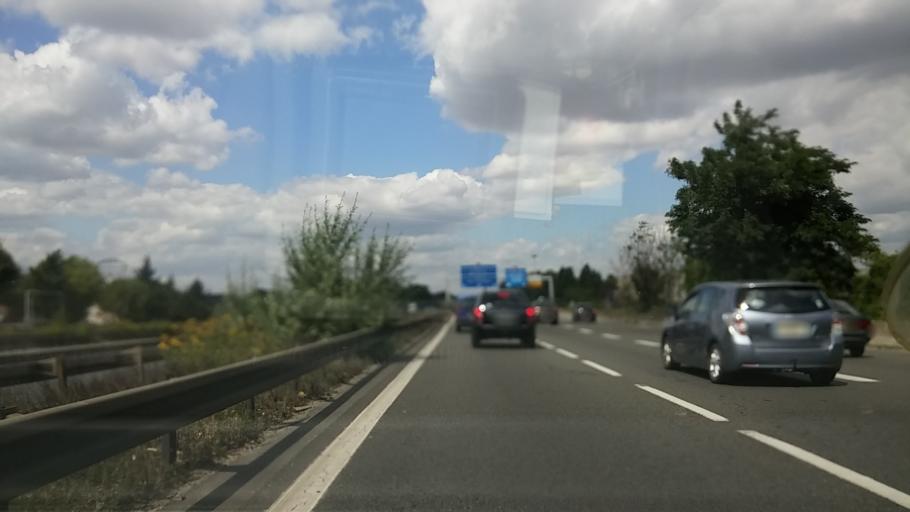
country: FR
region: Ile-de-France
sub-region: Departement de Seine-Saint-Denis
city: Le Blanc-Mesnil
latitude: 48.9445
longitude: 2.4773
